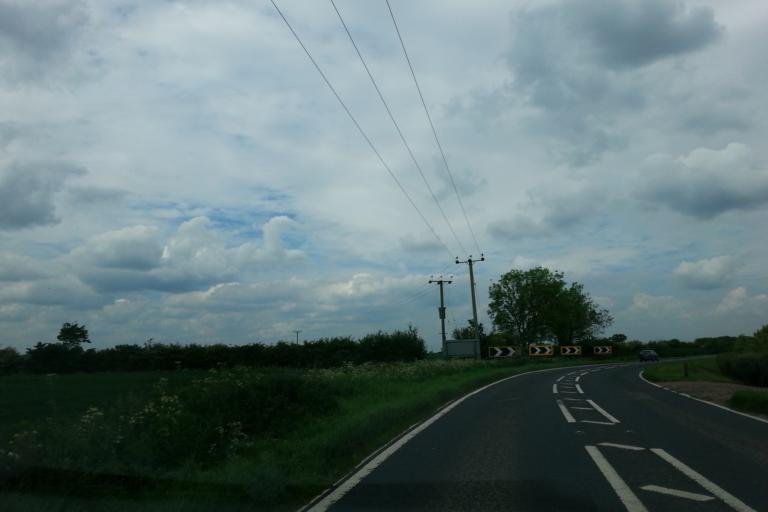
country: GB
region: England
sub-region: Cambridgeshire
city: Ramsey
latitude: 52.4172
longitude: -0.1073
